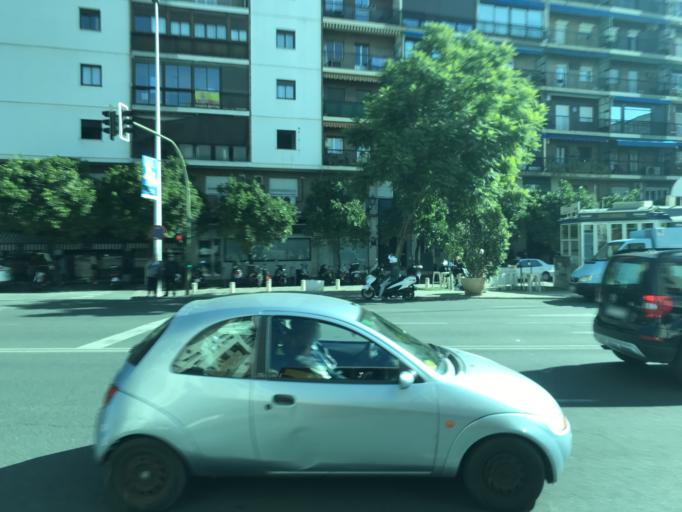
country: ES
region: Andalusia
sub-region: Provincia de Sevilla
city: Sevilla
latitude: 37.3886
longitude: -6.0022
